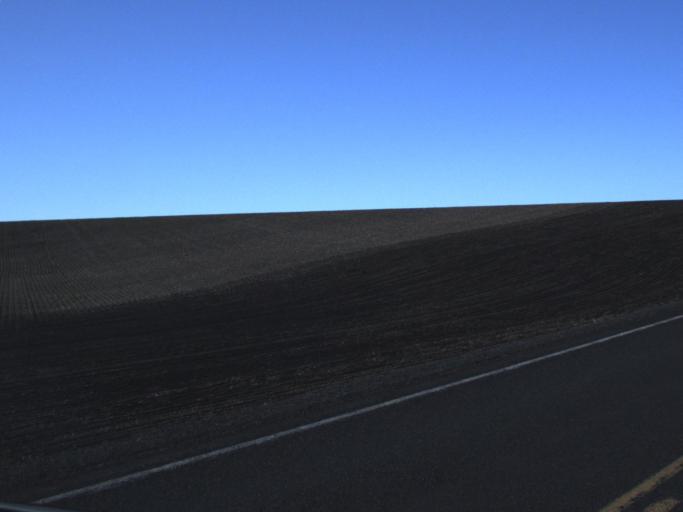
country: US
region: Washington
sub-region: Adams County
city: Ritzville
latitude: 47.0046
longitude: -118.3470
